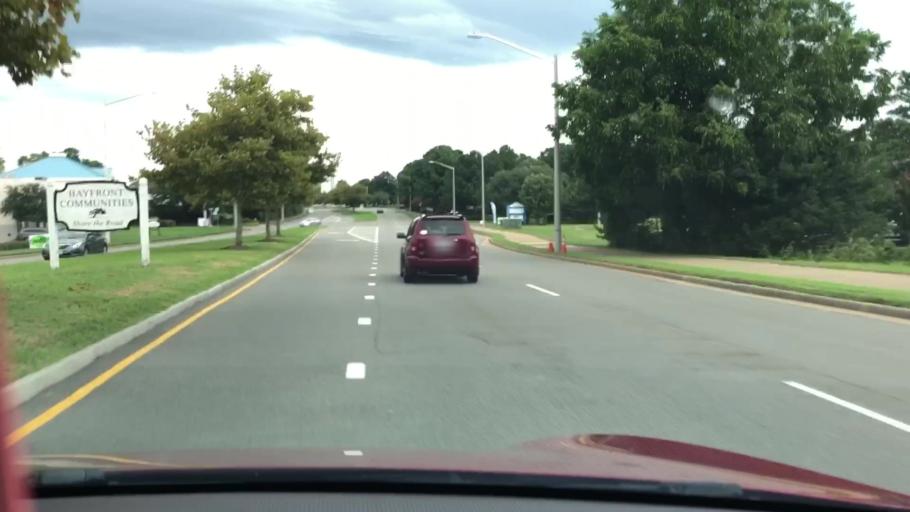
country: US
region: Virginia
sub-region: City of Virginia Beach
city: Virginia Beach
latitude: 36.9065
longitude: -76.0673
